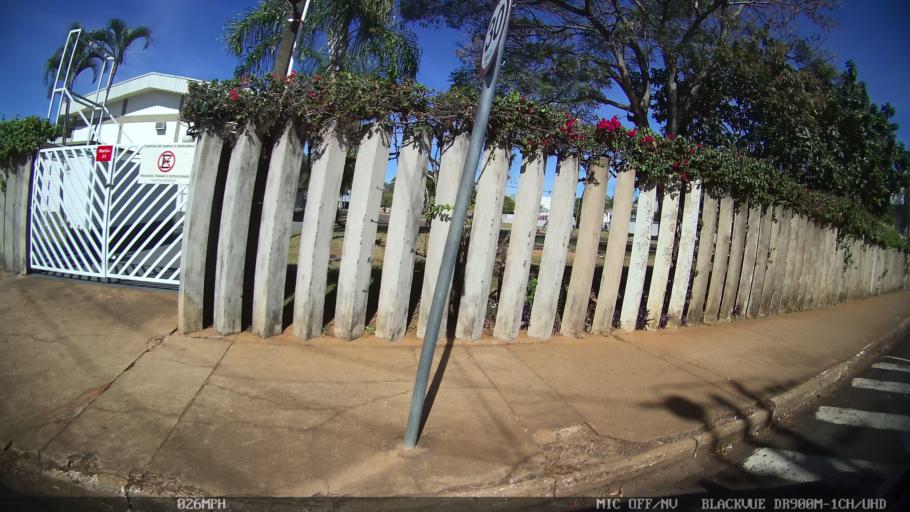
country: BR
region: Sao Paulo
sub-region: Franca
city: Franca
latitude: -20.5420
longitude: -47.3815
